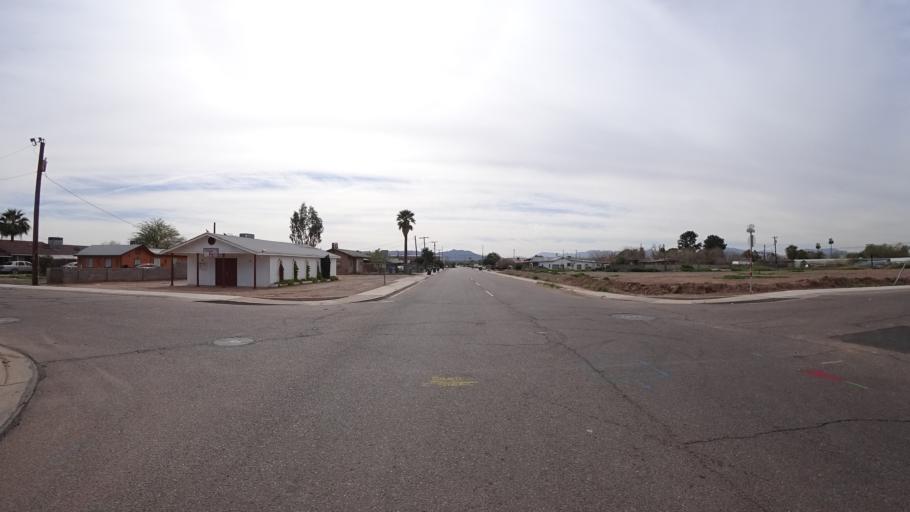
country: US
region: Arizona
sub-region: Maricopa County
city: Phoenix
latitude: 33.4350
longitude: -112.1260
